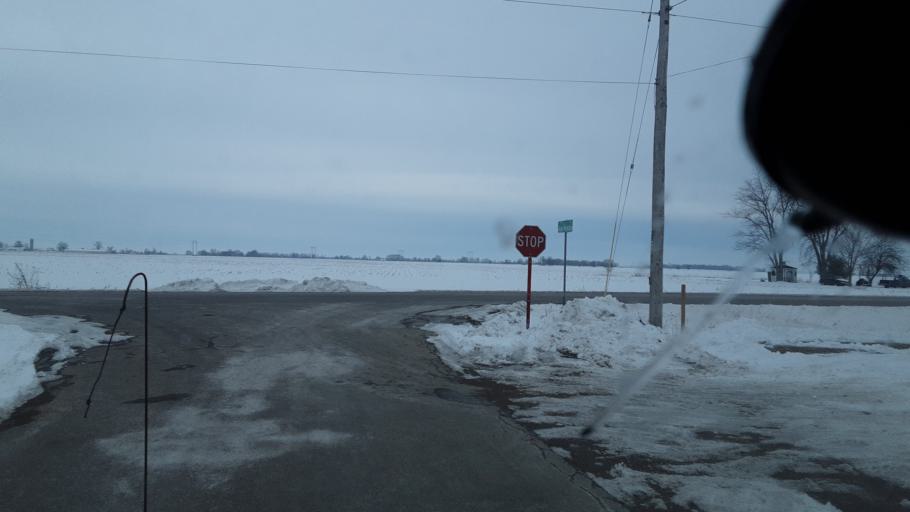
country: US
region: Ohio
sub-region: Union County
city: Marysville
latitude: 40.1154
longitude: -83.4254
